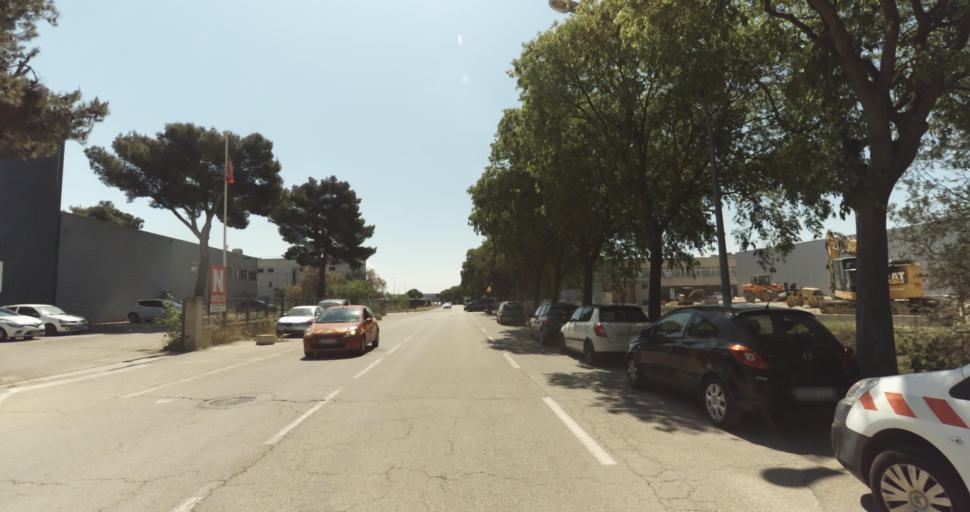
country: FR
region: Languedoc-Roussillon
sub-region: Departement du Gard
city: Milhaud
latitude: 43.8084
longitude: 4.3115
